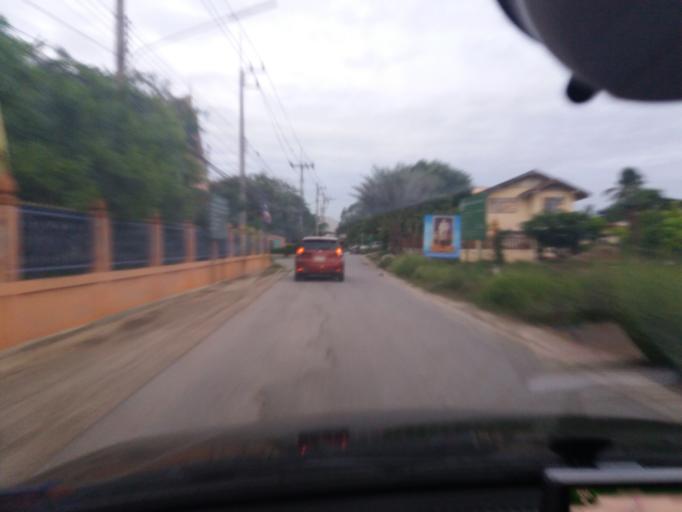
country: TH
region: Suphan Buri
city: Ban Sam Chuk
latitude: 14.7200
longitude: 100.0668
